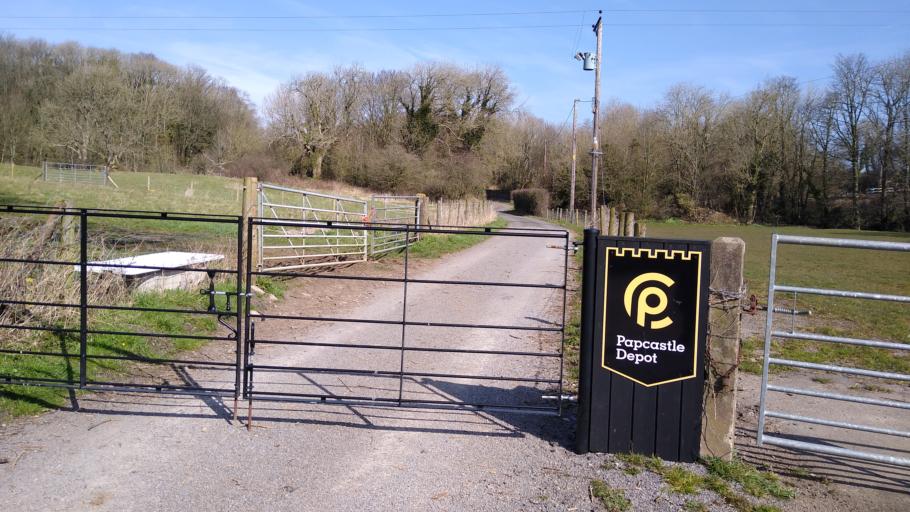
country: GB
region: England
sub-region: Cumbria
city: Dearham
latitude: 54.6707
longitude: -3.4121
